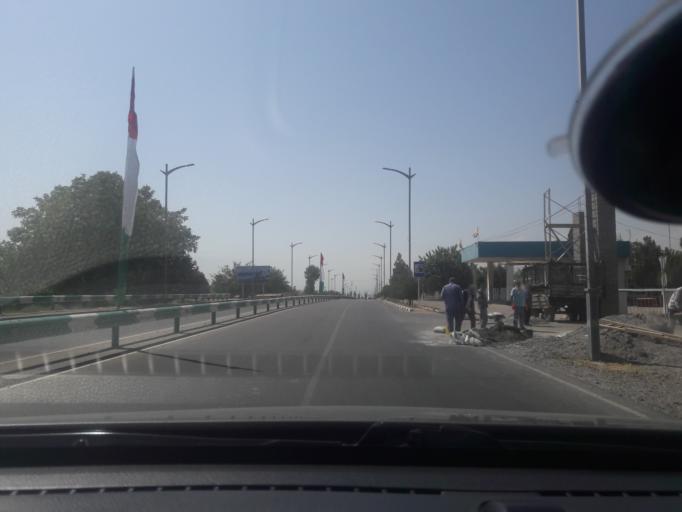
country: TJ
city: Shahrinav
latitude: 38.5639
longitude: 68.4044
